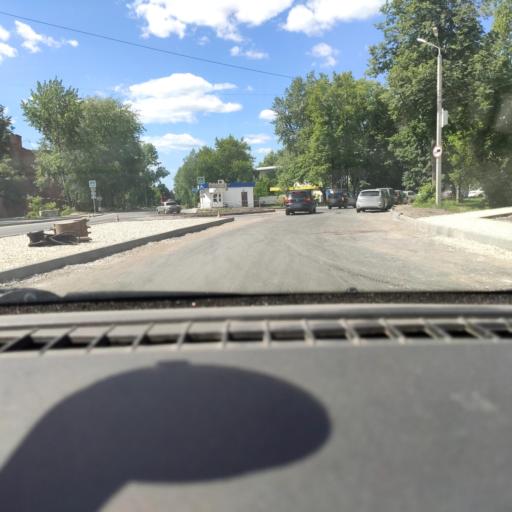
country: RU
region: Perm
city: Krasnokamsk
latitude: 58.0770
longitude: 55.7542
